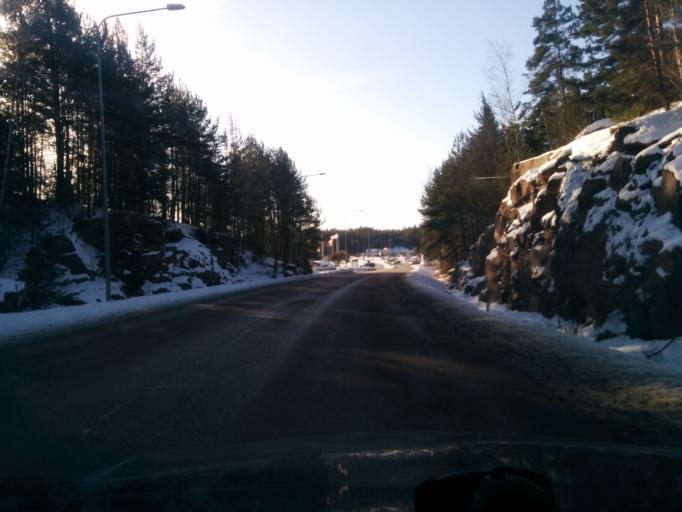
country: SE
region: Stockholm
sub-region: Taby Kommun
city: Taby
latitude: 59.4644
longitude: 18.1352
